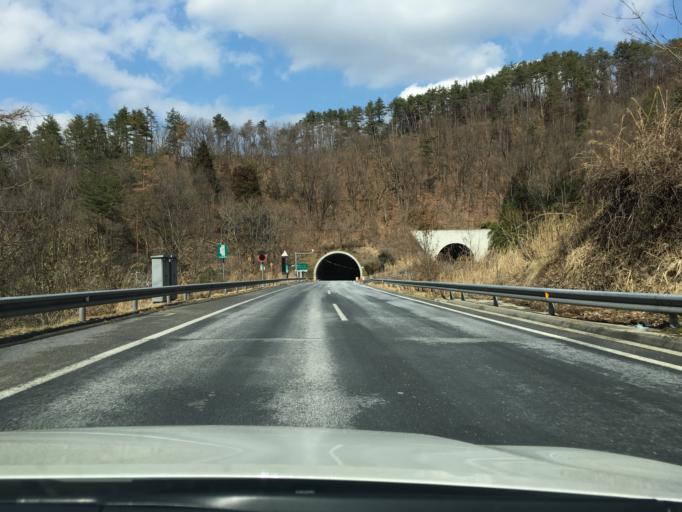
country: JP
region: Yamagata
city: Yamagata-shi
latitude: 38.2471
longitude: 140.3755
